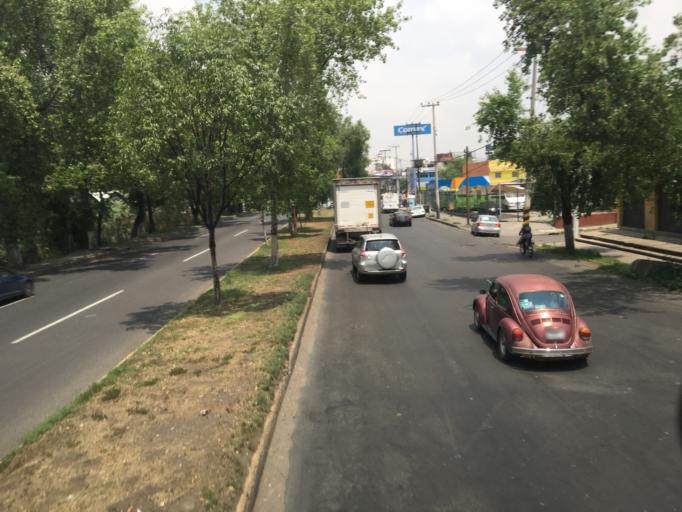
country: MX
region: Mexico
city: Tlalnepantla
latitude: 19.5322
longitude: -99.1783
